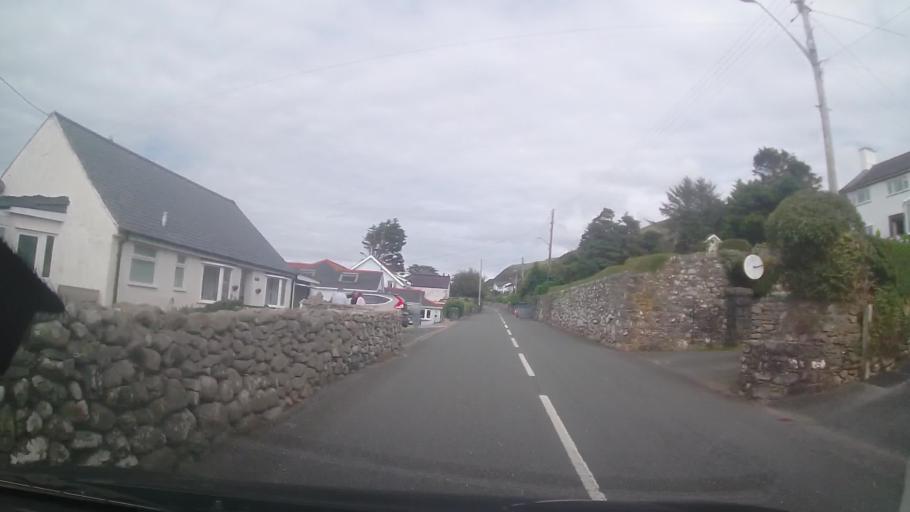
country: GB
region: Wales
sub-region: Gwynedd
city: Barmouth
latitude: 52.6726
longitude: -4.0810
